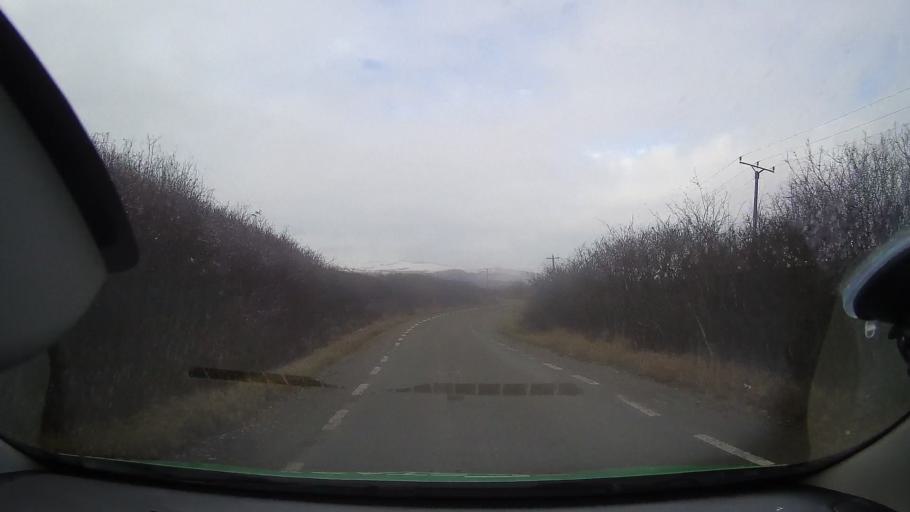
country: RO
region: Mures
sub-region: Comuna Atintis
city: Atintis
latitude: 46.4063
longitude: 24.0865
